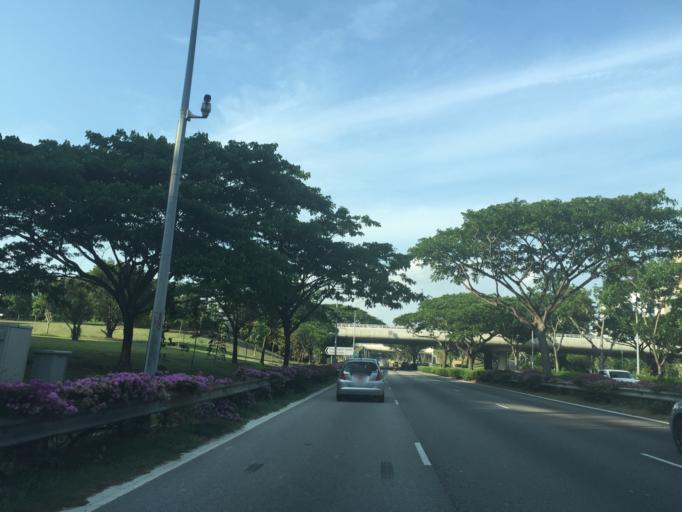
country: SG
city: Singapore
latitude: 1.3408
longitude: 103.9458
